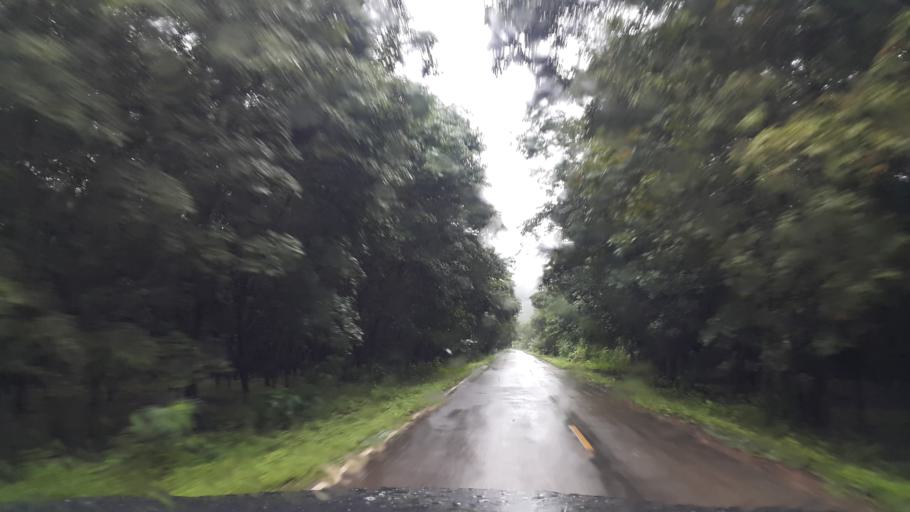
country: TH
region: Phayao
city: Phu Sang
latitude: 19.6143
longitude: 100.4070
